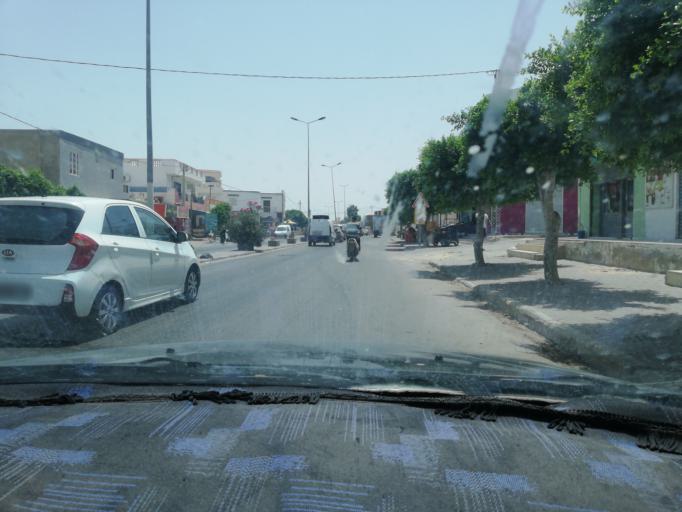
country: TN
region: Qabis
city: Gabes
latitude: 33.6217
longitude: 10.2829
